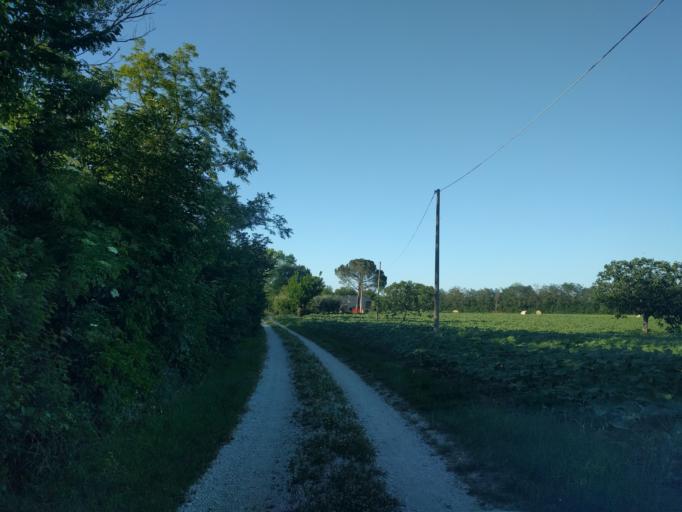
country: IT
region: The Marches
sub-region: Provincia di Pesaro e Urbino
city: Montemaggiore al Metauro
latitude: 43.7505
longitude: 12.9579
